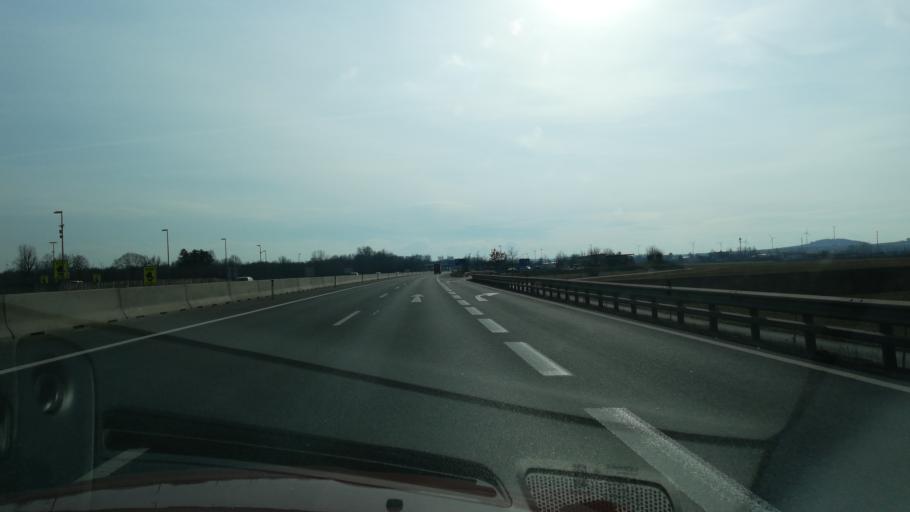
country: AT
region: Lower Austria
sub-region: Politischer Bezirk Sankt Polten
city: Herzogenburg
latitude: 48.3131
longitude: 15.7164
